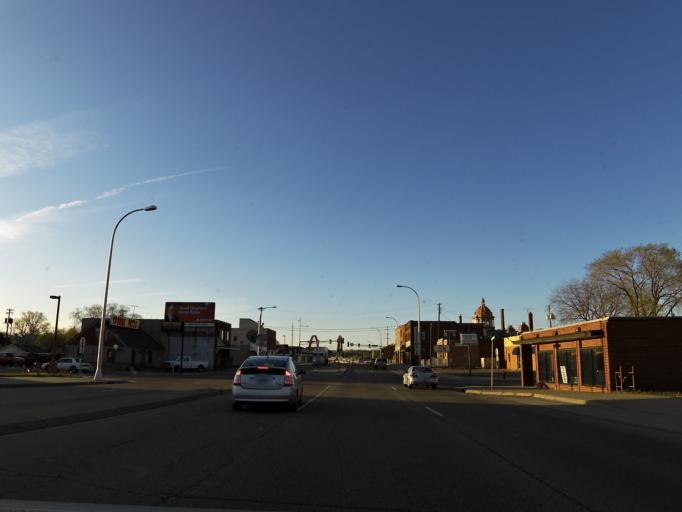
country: US
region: Minnesota
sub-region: Dakota County
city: Hastings
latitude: 44.7408
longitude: -92.8525
